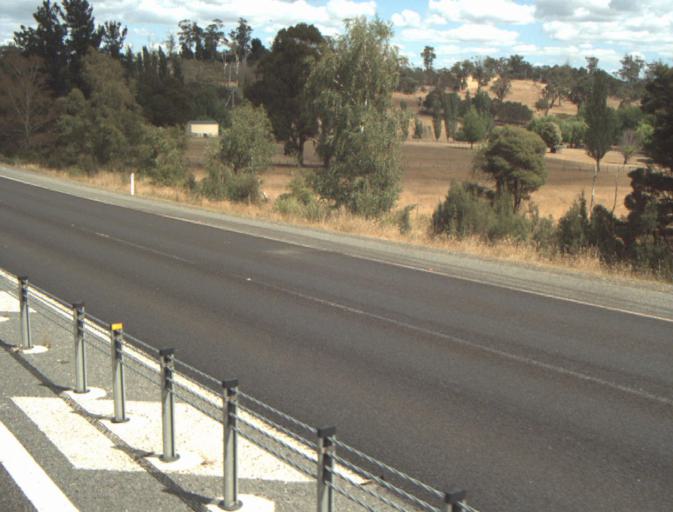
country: AU
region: Tasmania
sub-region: Launceston
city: Mayfield
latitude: -41.2929
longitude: 147.0477
